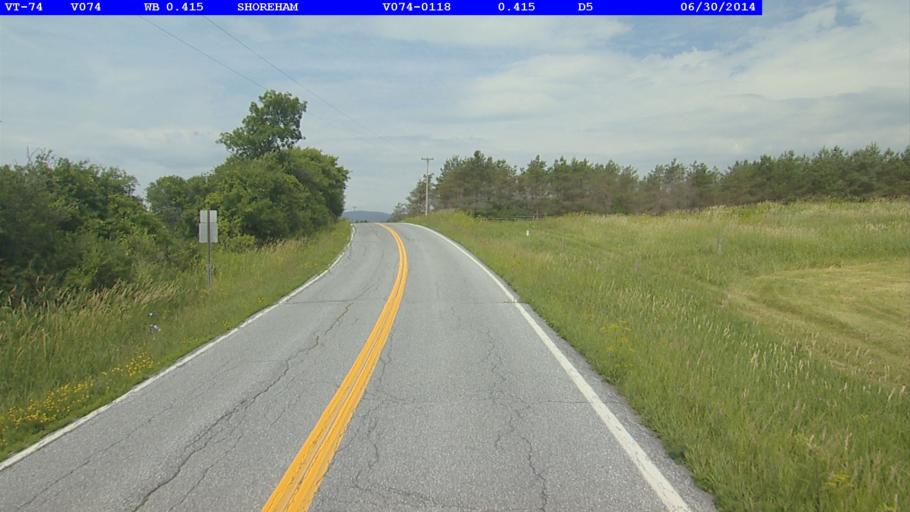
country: US
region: New York
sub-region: Essex County
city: Ticonderoga
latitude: 43.8568
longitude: -73.3687
